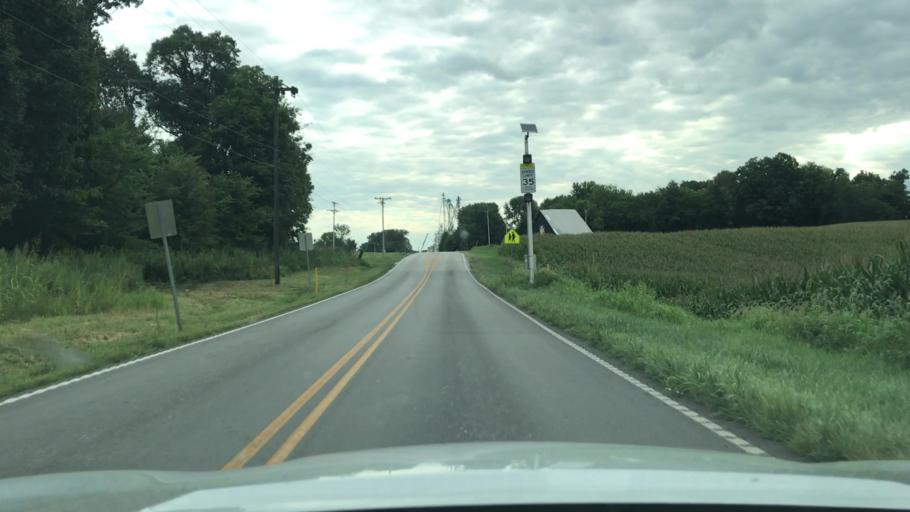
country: US
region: Kentucky
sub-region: Todd County
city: Elkton
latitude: 36.7491
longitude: -87.1733
